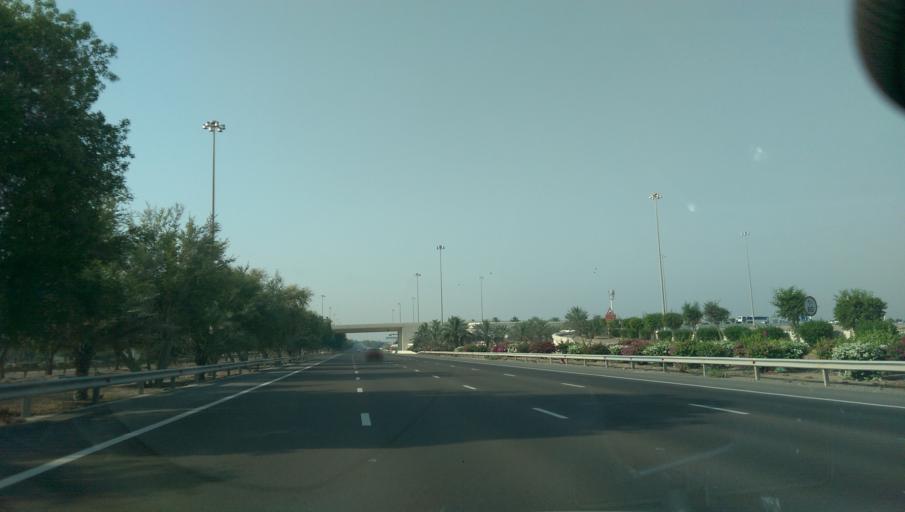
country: AE
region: Abu Dhabi
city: Abu Dhabi
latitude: 24.4663
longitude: 54.6769
